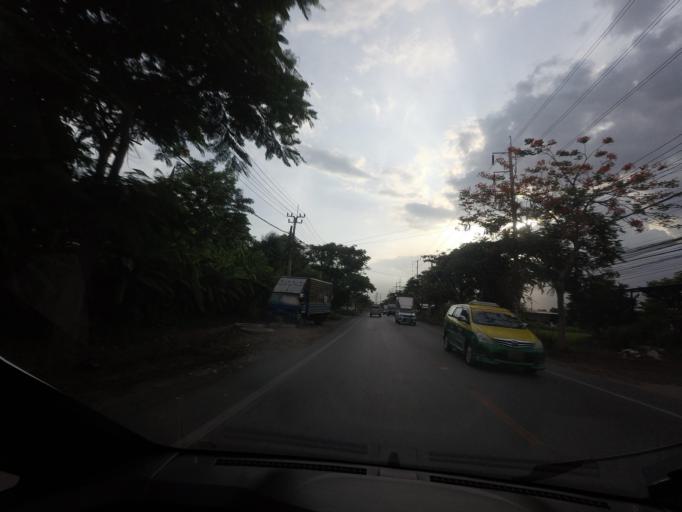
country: TH
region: Bangkok
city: Nong Chok
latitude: 13.8547
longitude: 100.8104
